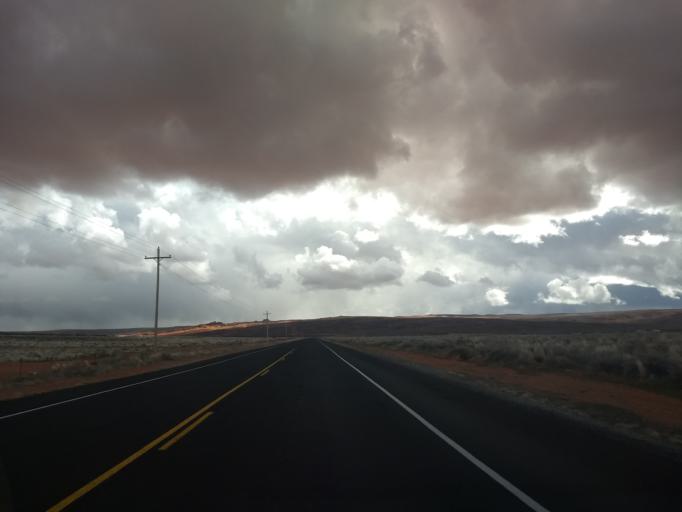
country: US
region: Utah
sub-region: Washington County
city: Hurricane
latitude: 37.1309
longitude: -113.3927
